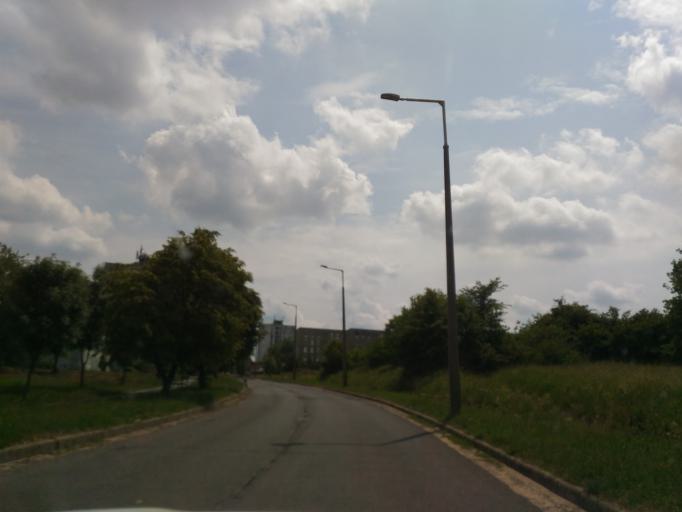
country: HU
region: Baranya
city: Komlo
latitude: 46.1921
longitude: 18.2299
